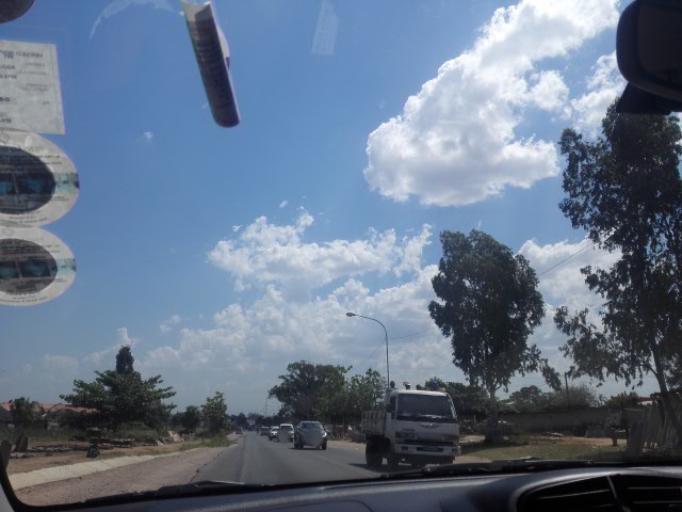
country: MZ
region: Maputo
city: Matola
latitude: -25.9688
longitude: 32.4428
